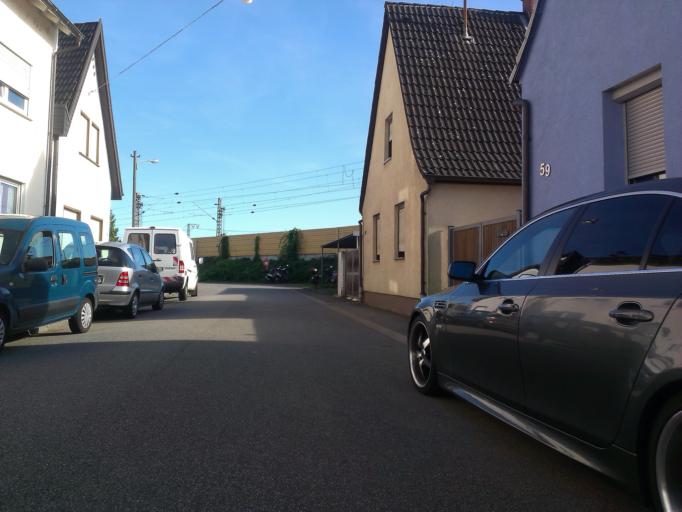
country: DE
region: Baden-Wuerttemberg
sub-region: Karlsruhe Region
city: Edingen-Neckarhausen
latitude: 49.4370
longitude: 8.5768
